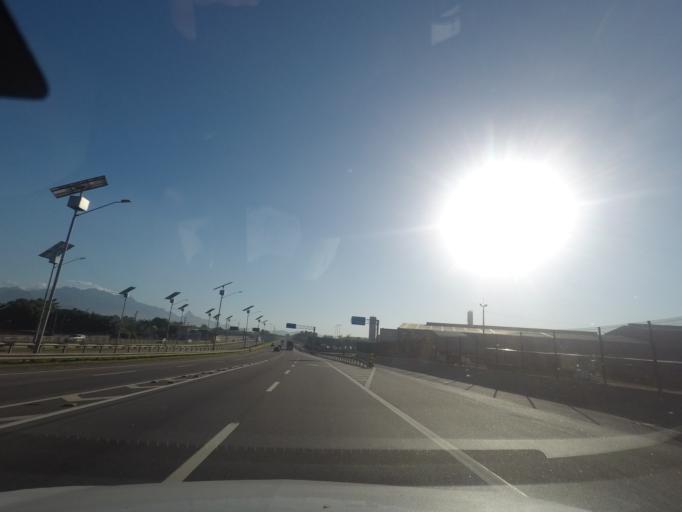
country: BR
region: Rio de Janeiro
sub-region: Duque De Caxias
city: Duque de Caxias
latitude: -22.6723
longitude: -43.2818
